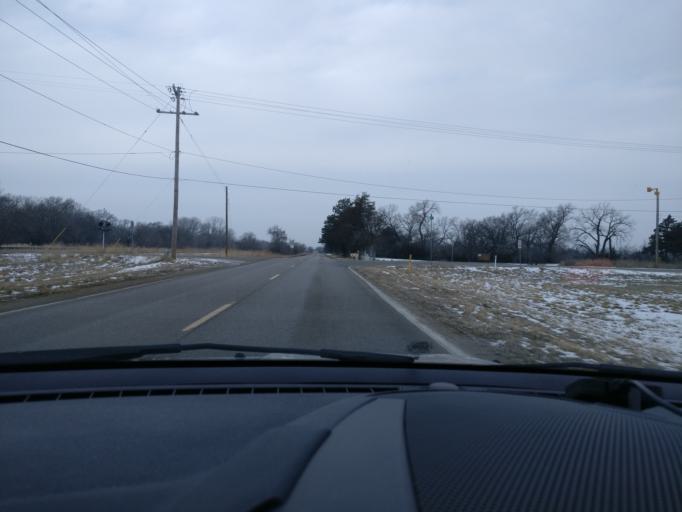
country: US
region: Nebraska
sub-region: Dodge County
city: Fremont
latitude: 41.4477
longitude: -96.5581
